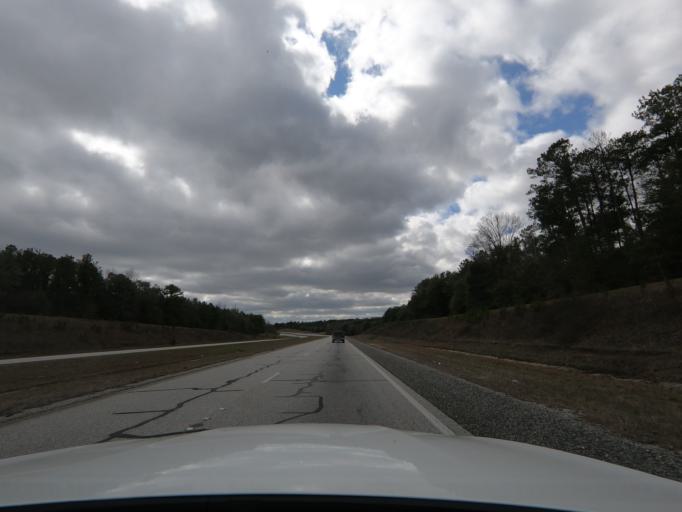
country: US
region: Alabama
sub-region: Russell County
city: Ladonia
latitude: 32.3051
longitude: -85.1791
